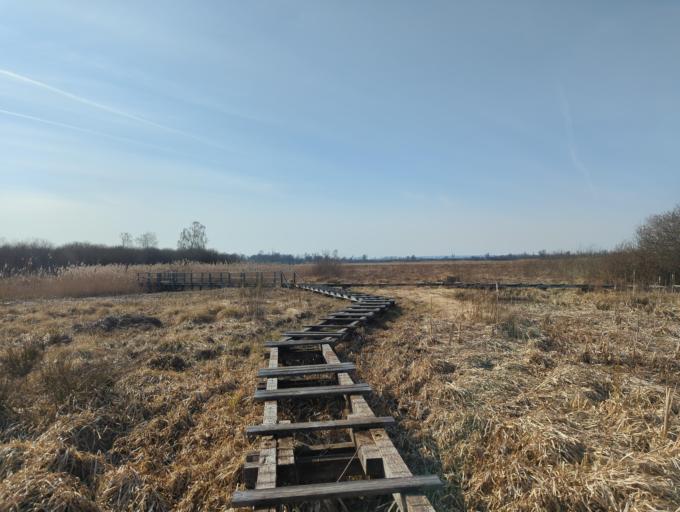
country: DE
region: Bavaria
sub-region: Swabia
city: Leipheim
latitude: 48.4814
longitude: 10.2143
